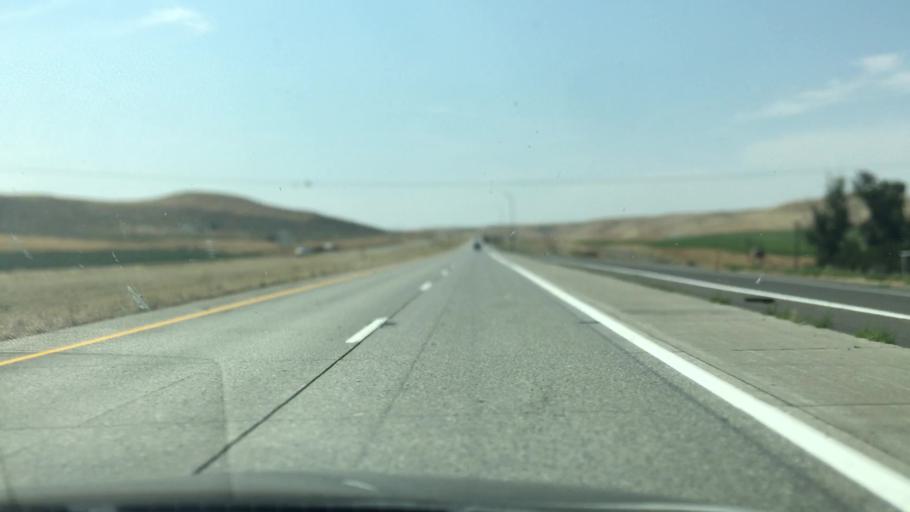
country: US
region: Idaho
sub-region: Elmore County
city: Glenns Ferry
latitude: 42.9621
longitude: -115.3125
